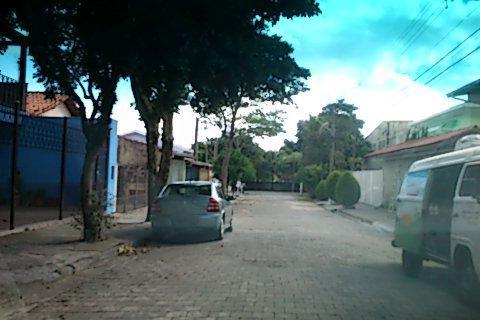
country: BR
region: Sao Paulo
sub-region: Sao Jose Dos Campos
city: Sao Jose dos Campos
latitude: -23.2408
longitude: -45.8841
